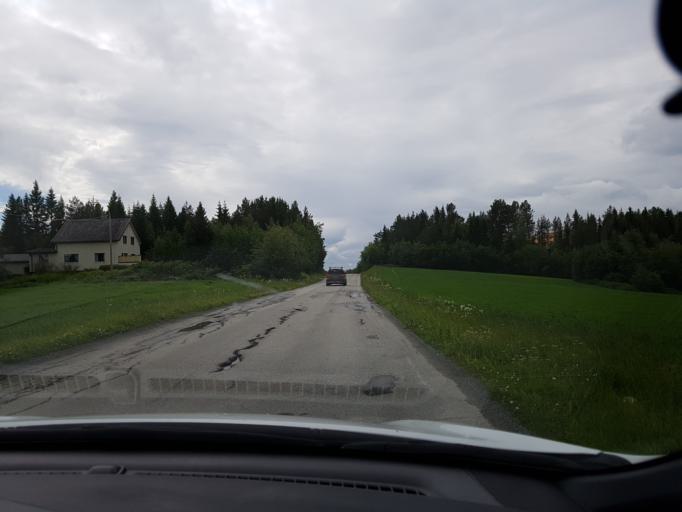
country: NO
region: Nord-Trondelag
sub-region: Frosta
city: Frosta
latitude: 63.6048
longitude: 10.7356
